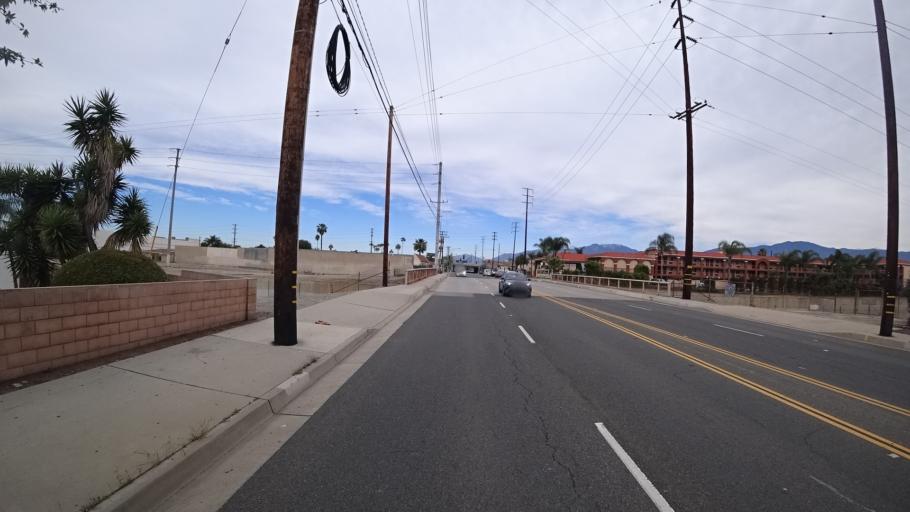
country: US
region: California
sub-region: Los Angeles County
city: West Puente Valley
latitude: 34.0666
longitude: -117.9715
